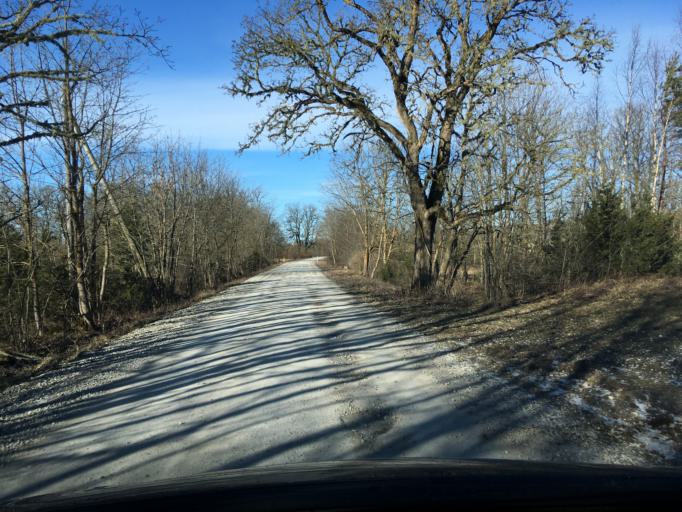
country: EE
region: Laeaene
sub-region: Lihula vald
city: Lihula
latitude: 58.5679
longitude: 23.6659
